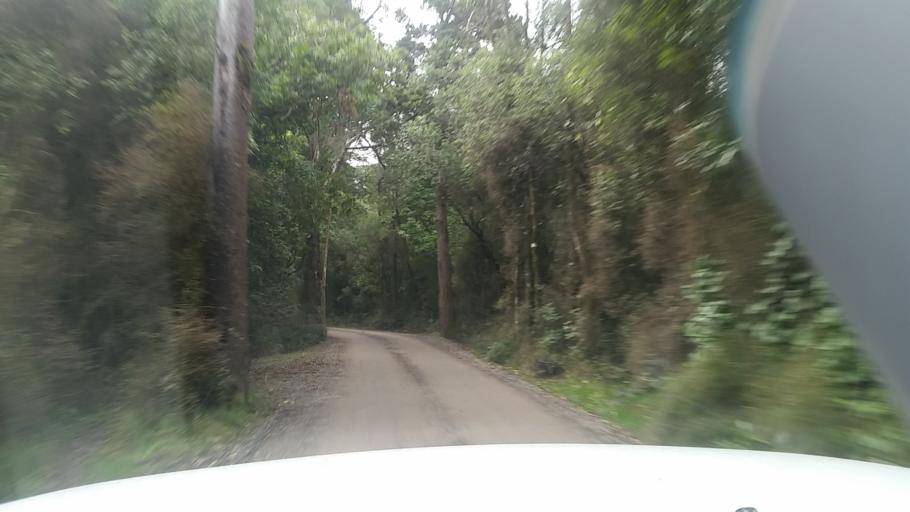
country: NZ
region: Canterbury
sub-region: Christchurch City
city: Christchurch
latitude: -43.7673
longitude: 172.7130
